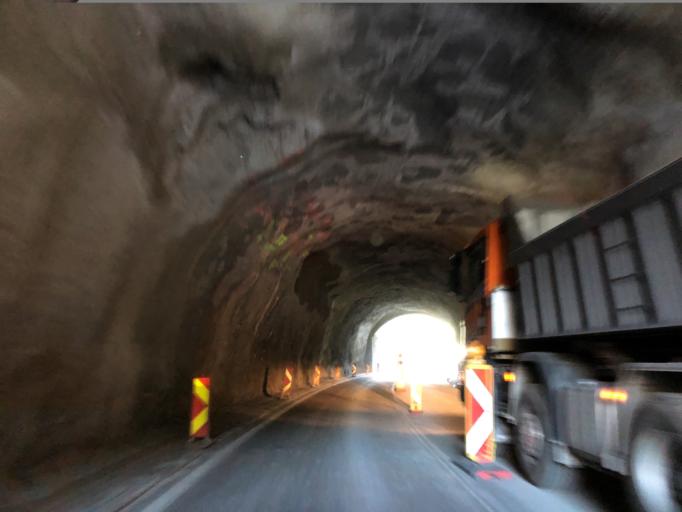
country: AT
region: Tyrol
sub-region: Politischer Bezirk Imst
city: Soelden
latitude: 46.9901
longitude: 11.0114
